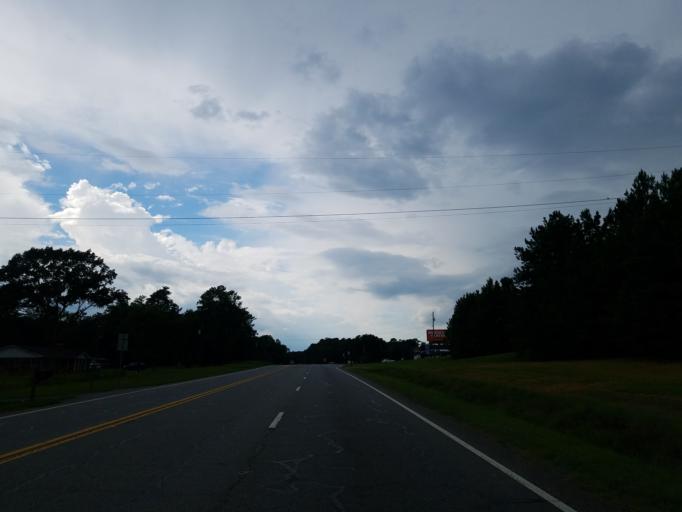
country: US
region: Georgia
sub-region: Bartow County
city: Adairsville
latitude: 34.3427
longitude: -84.9089
